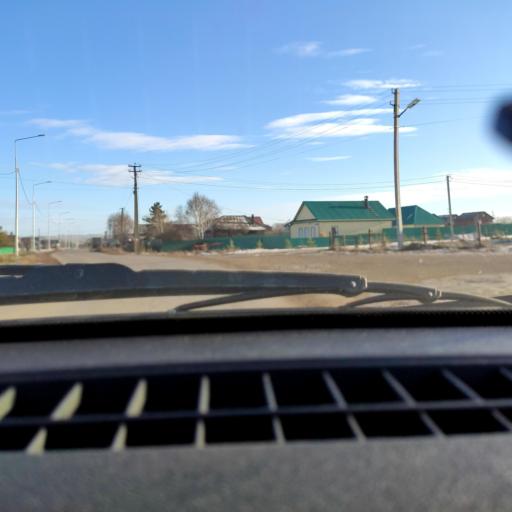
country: RU
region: Bashkortostan
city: Kabakovo
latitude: 54.5020
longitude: 55.9157
